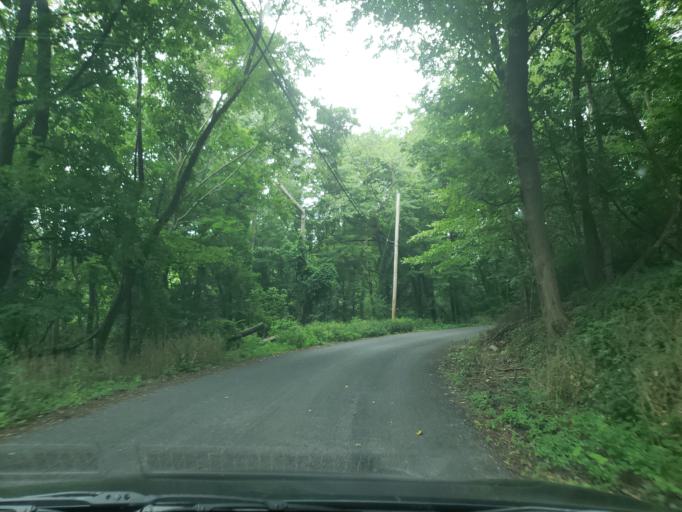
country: US
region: Pennsylvania
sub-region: Allegheny County
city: Ben Avon
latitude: 40.5130
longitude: -80.0808
